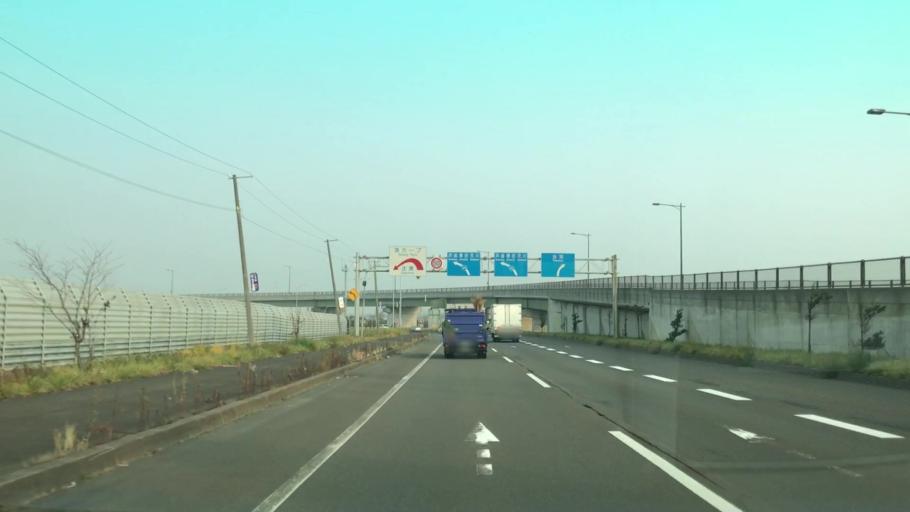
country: JP
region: Hokkaido
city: Ishikari
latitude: 43.1775
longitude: 141.3480
